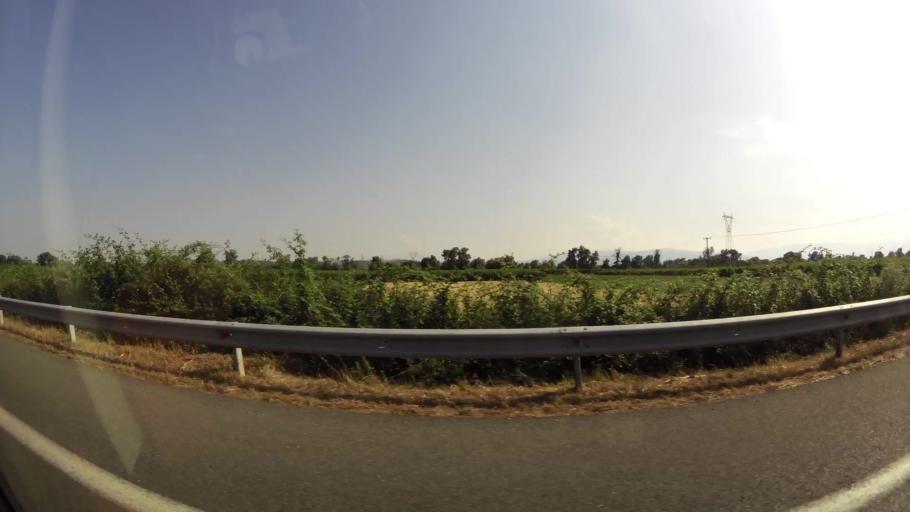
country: GR
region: Central Macedonia
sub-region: Nomos Imathias
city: Agkathia
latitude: 40.5862
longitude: 22.4764
